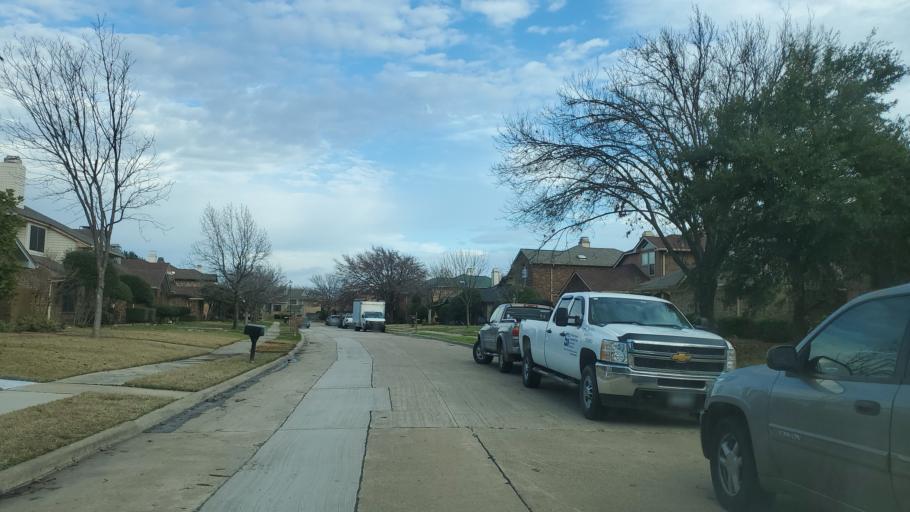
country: US
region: Texas
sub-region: Dallas County
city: Carrollton
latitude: 32.9962
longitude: -96.8996
